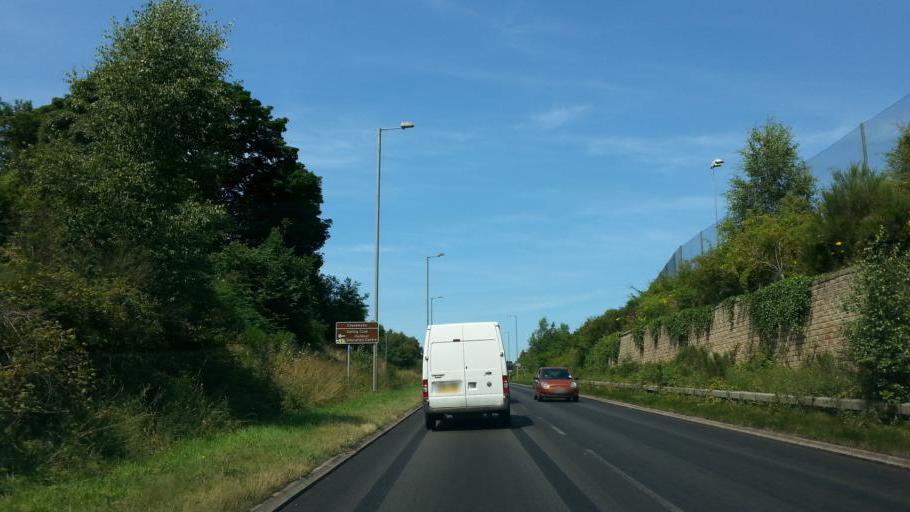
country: GB
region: England
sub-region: Staffordshire
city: Chasetown
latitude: 52.6667
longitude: -1.9386
